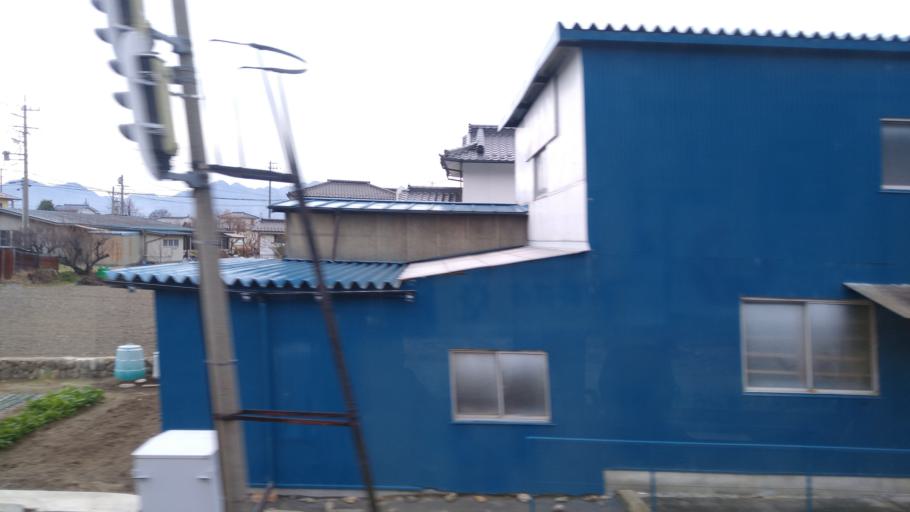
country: JP
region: Nagano
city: Ueda
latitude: 36.4153
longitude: 138.2136
